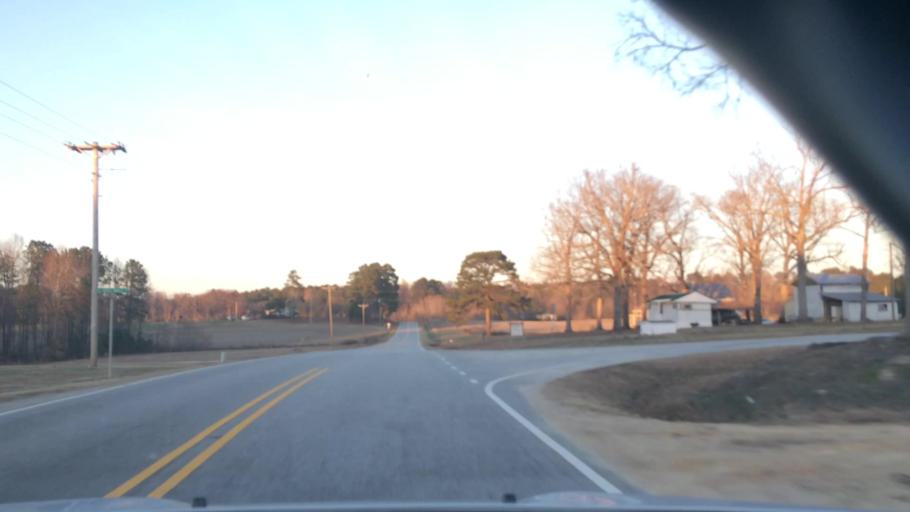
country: US
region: North Carolina
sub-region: Franklin County
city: Youngsville
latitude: 35.9820
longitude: -78.4196
